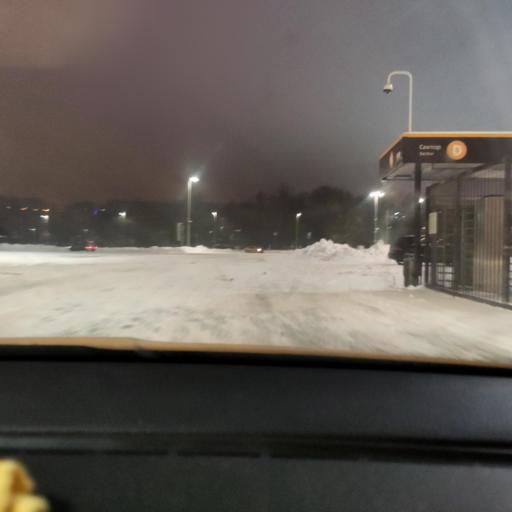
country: RU
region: Moscow
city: Luzhniki
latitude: 55.7150
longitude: 37.5563
